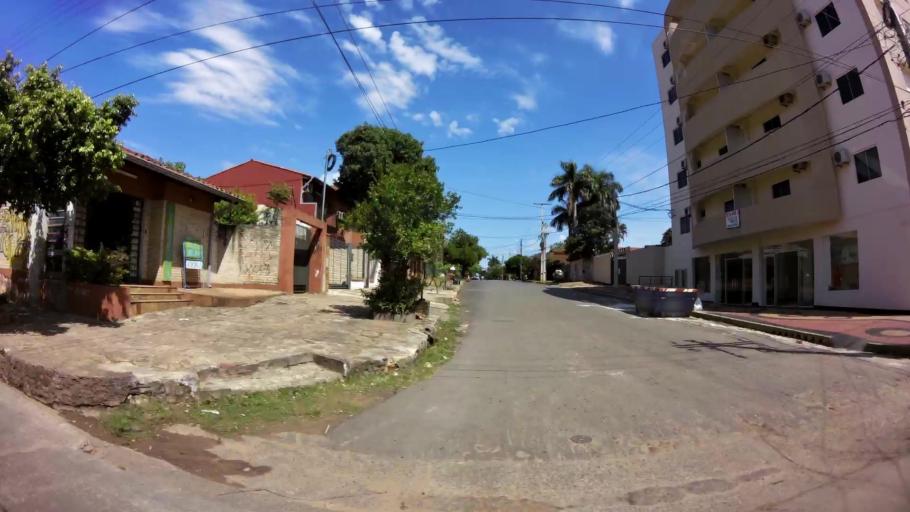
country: PY
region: Central
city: San Lorenzo
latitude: -25.2694
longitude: -57.4956
